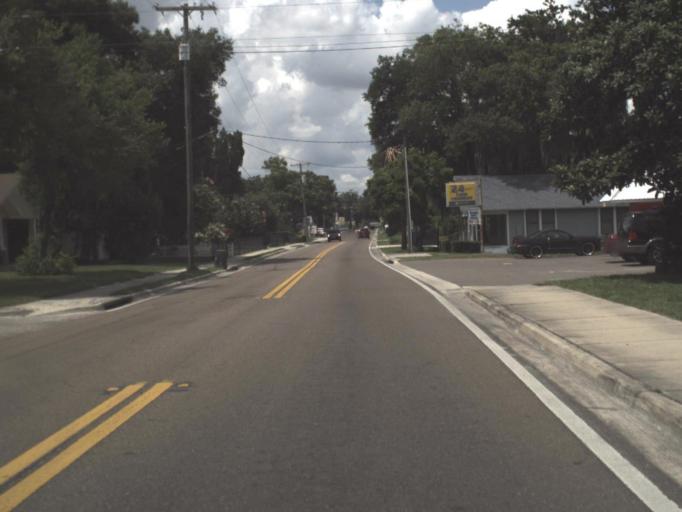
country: US
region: Florida
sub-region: Hillsborough County
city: Plant City
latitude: 28.0252
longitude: -82.1256
